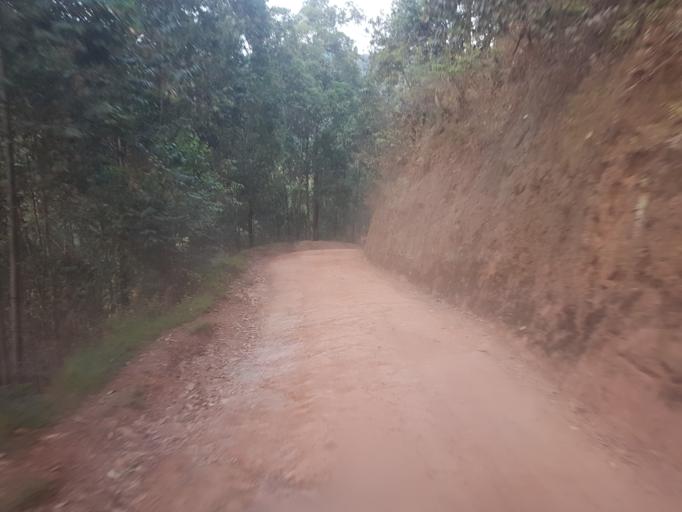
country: UG
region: Western Region
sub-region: Kanungu District
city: Kanungu
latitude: -0.9601
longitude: 29.8369
